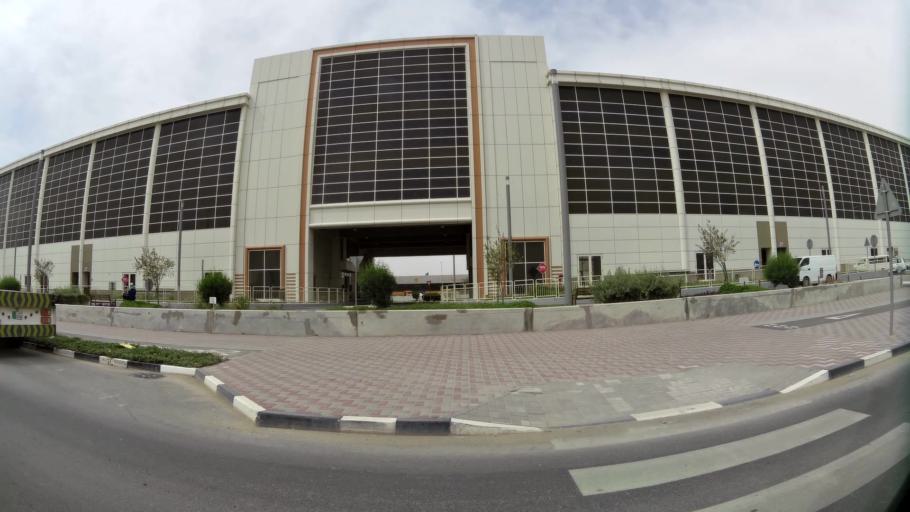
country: QA
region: Baladiyat ar Rayyan
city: Ar Rayyan
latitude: 25.1983
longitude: 51.4523
